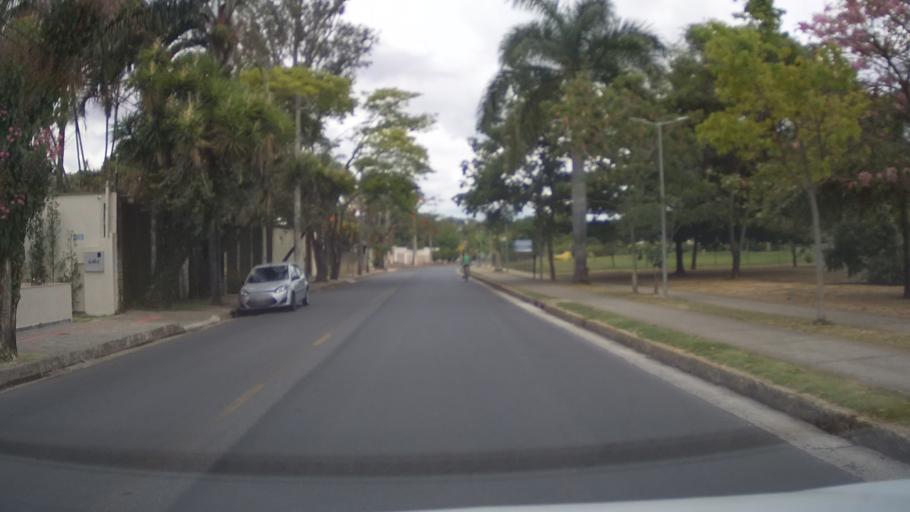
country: BR
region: Minas Gerais
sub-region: Belo Horizonte
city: Belo Horizonte
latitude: -19.8561
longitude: -43.9948
